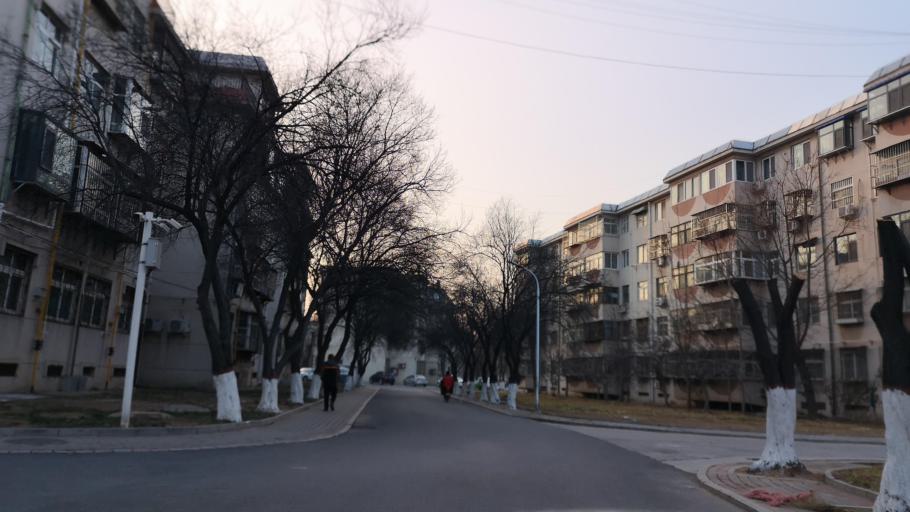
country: CN
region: Henan Sheng
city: Zhongyuanlu
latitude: 35.7687
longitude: 115.0805
